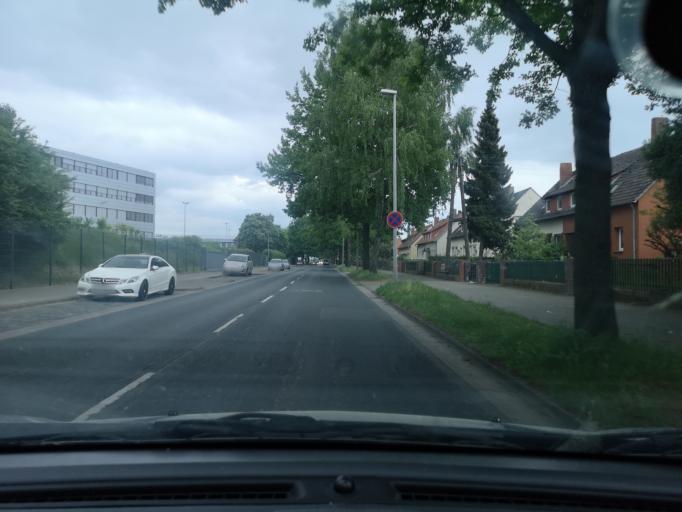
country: DE
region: Lower Saxony
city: Langenhagen
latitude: 52.4171
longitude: 9.6850
